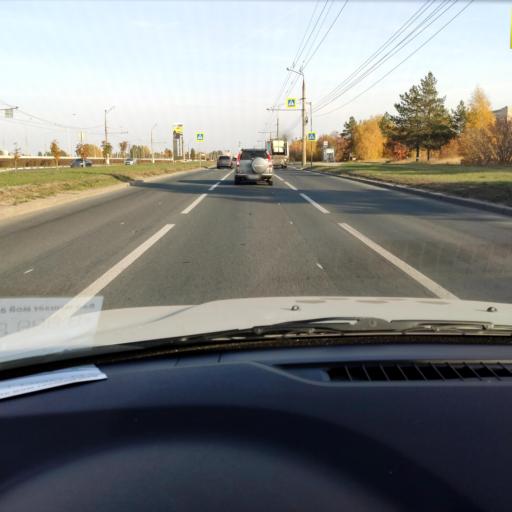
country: RU
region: Samara
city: Tol'yatti
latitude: 53.5545
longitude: 49.2742
